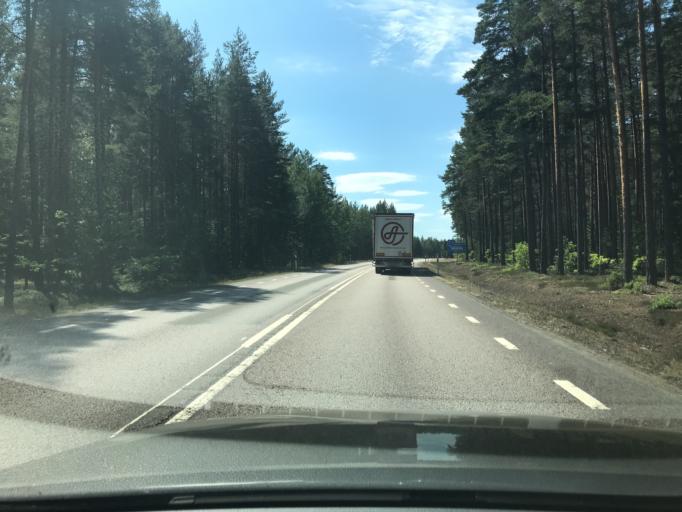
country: SE
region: Kalmar
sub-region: Hultsfreds Kommun
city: Malilla
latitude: 57.3848
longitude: 15.7525
